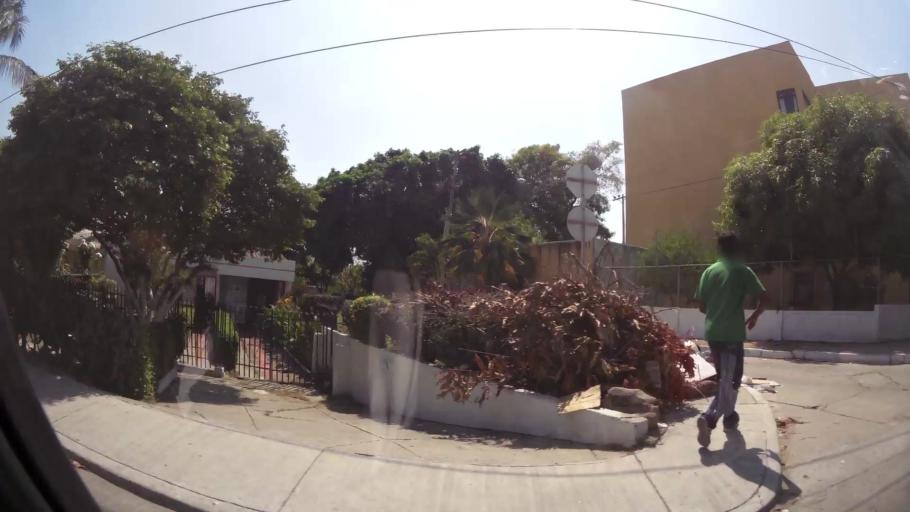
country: CO
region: Bolivar
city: Cartagena
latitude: 10.3941
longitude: -75.4908
